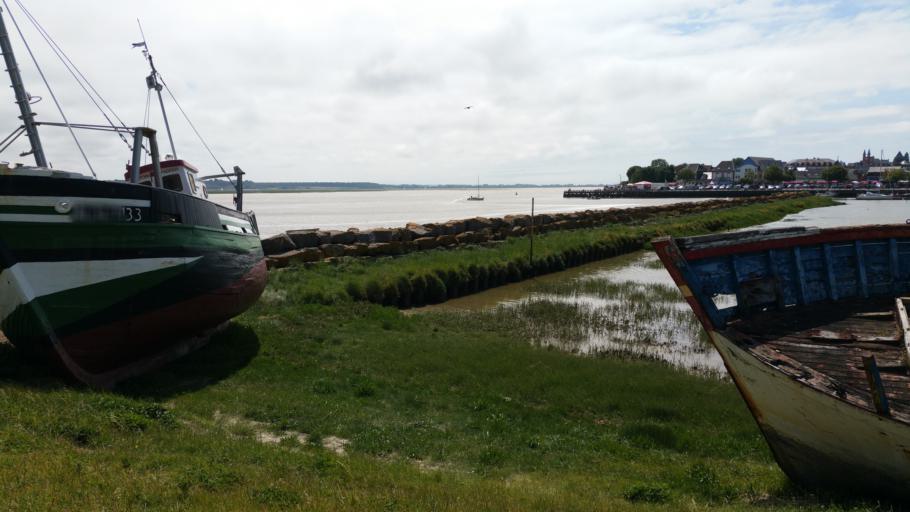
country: FR
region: Picardie
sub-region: Departement de la Somme
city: Le Crotoy
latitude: 50.2166
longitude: 1.6332
